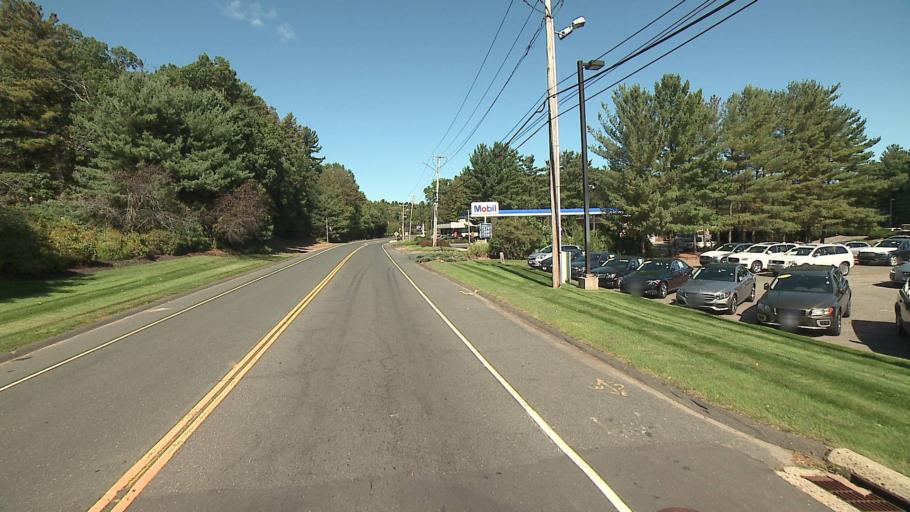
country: US
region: Connecticut
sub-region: Hartford County
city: Weatogue
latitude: 41.8521
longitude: -72.8131
